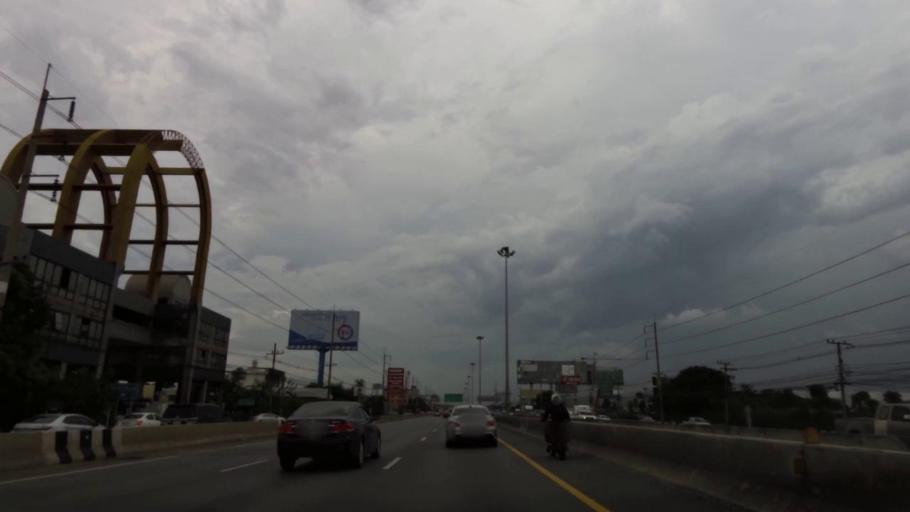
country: TH
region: Pathum Thani
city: Khlong Luang
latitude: 14.0897
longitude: 100.6184
